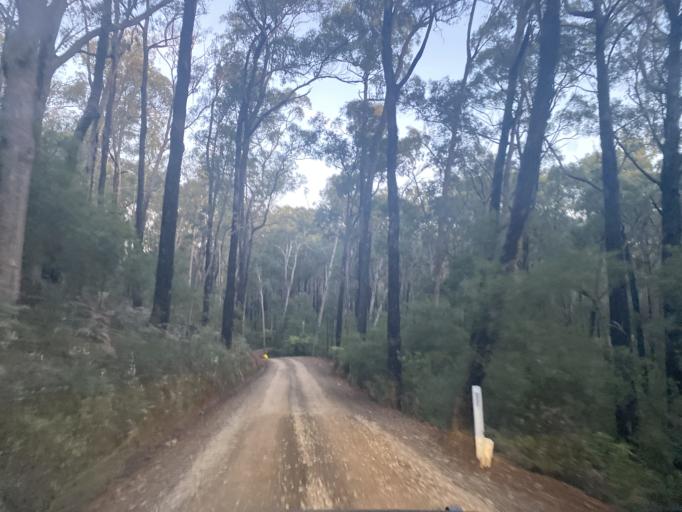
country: AU
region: Victoria
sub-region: Yarra Ranges
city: Healesville
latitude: -37.4471
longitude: 145.4812
